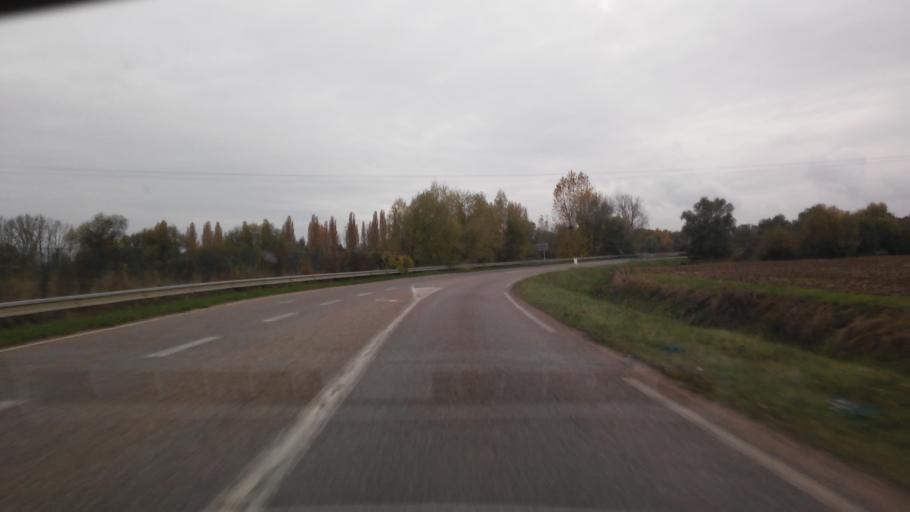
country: FR
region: Lorraine
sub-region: Departement de la Moselle
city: Ay-sur-Moselle
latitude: 49.2432
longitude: 6.1961
